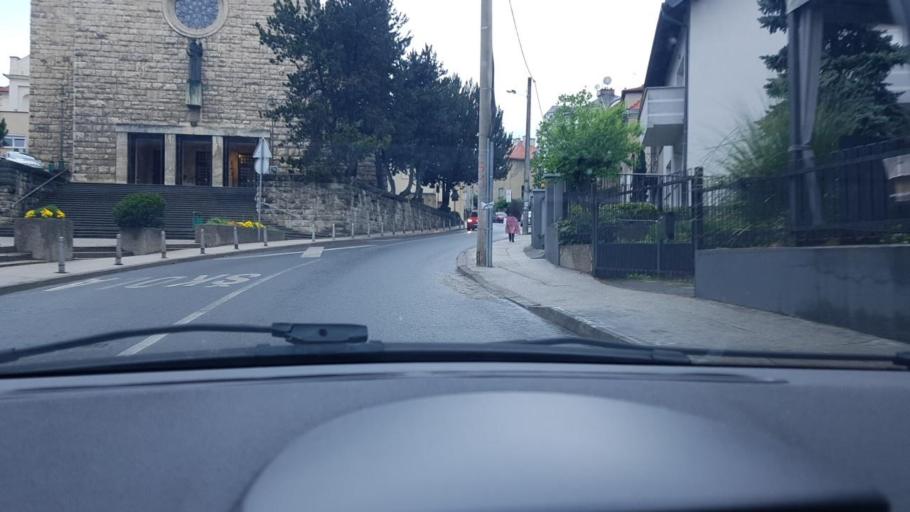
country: HR
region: Grad Zagreb
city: Zagreb - Centar
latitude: 45.8159
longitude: 15.9420
